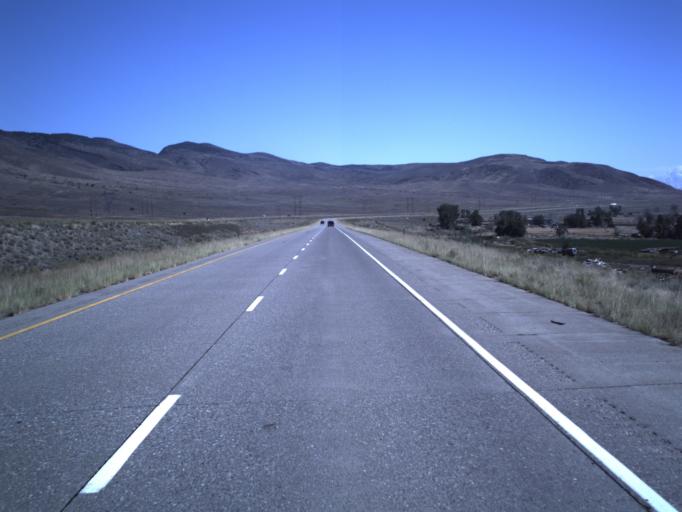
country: US
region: Utah
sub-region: Sevier County
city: Monroe
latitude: 38.6456
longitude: -112.2162
